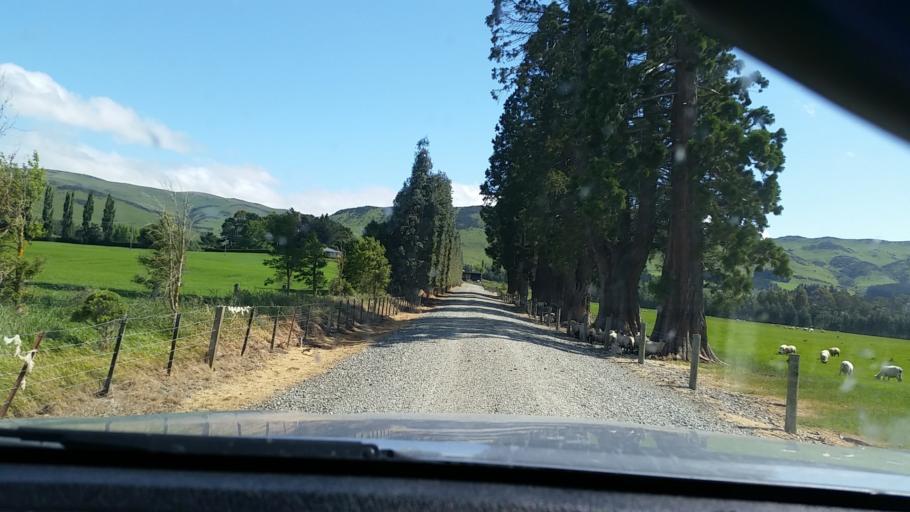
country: NZ
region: Southland
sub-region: Southland District
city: Winton
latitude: -45.9100
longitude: 168.5640
